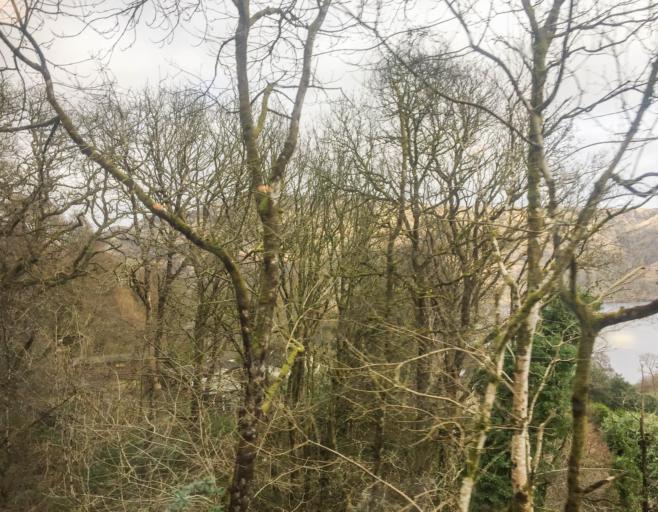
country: GB
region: Scotland
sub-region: Argyll and Bute
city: Garelochhead
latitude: 56.2192
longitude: -4.6993
